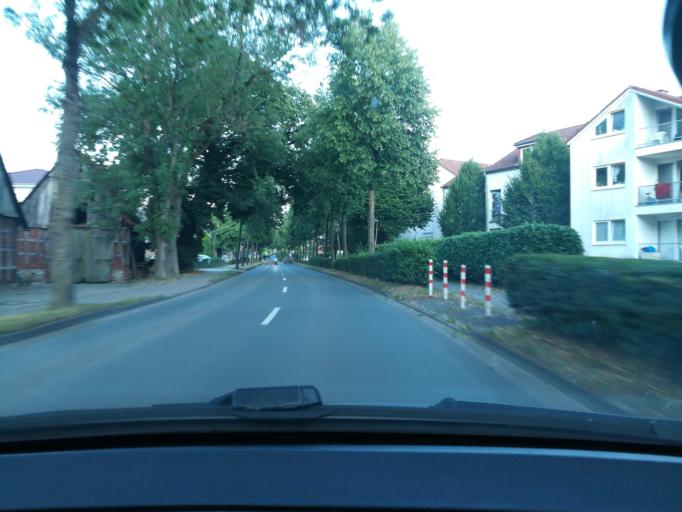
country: DE
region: North Rhine-Westphalia
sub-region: Regierungsbezirk Munster
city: Lienen
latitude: 52.1455
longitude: 7.9799
